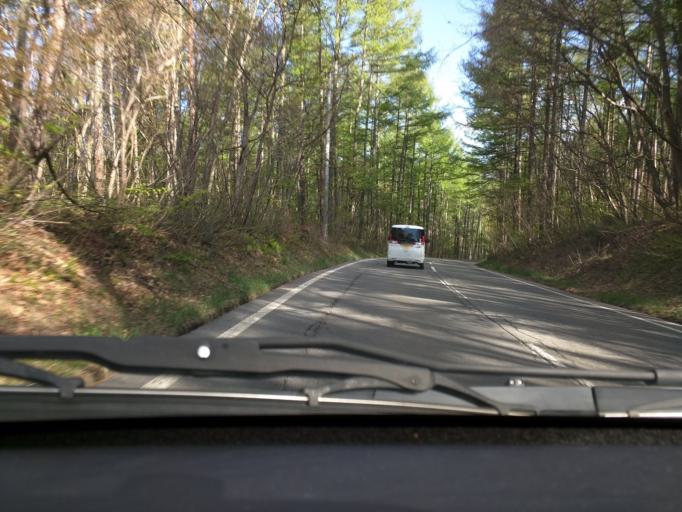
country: JP
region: Nagano
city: Nagano-shi
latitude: 36.7115
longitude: 138.1158
